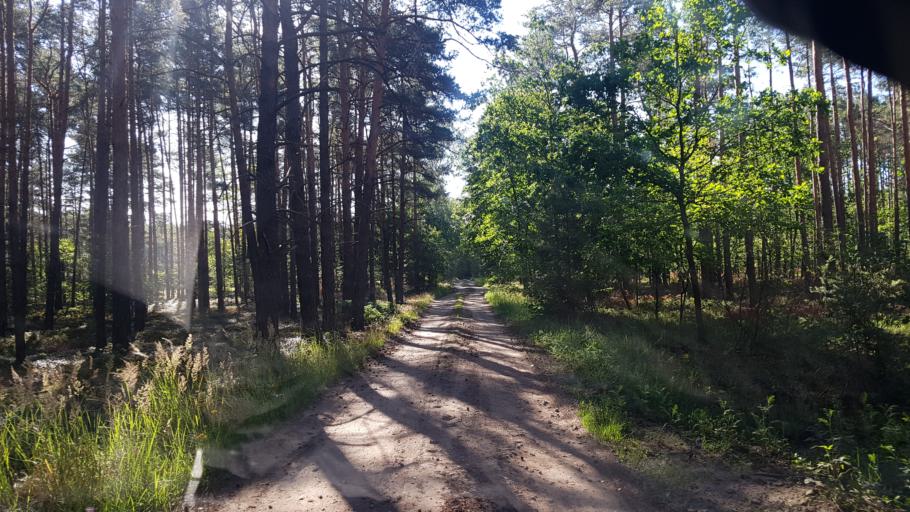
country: DE
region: Brandenburg
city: Sallgast
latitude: 51.6022
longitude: 13.8073
